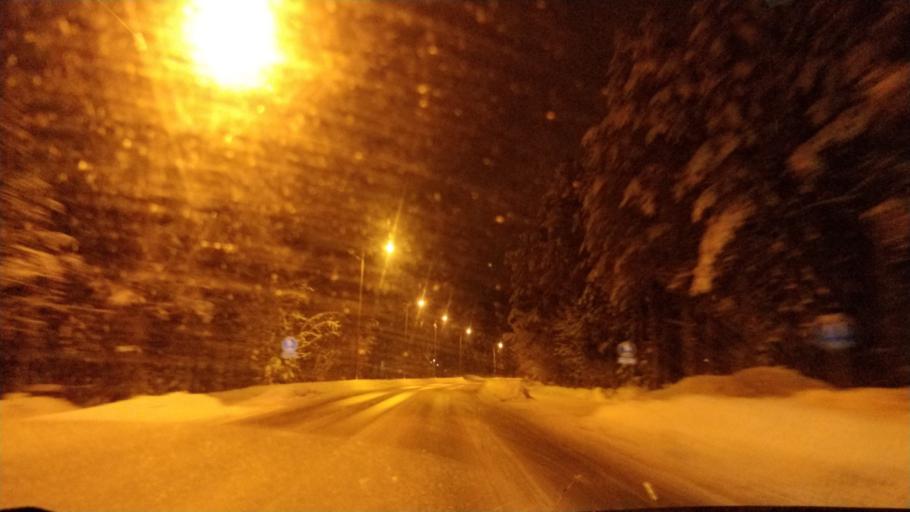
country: FI
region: Lapland
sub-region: Rovaniemi
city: Rovaniemi
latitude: 66.3779
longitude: 25.3818
